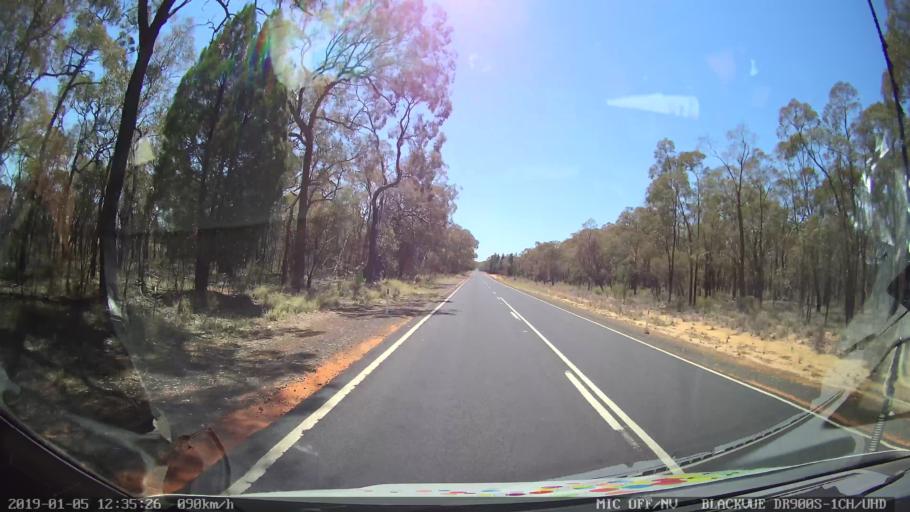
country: AU
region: New South Wales
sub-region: Warrumbungle Shire
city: Coonabarabran
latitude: -31.2096
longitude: 149.4256
